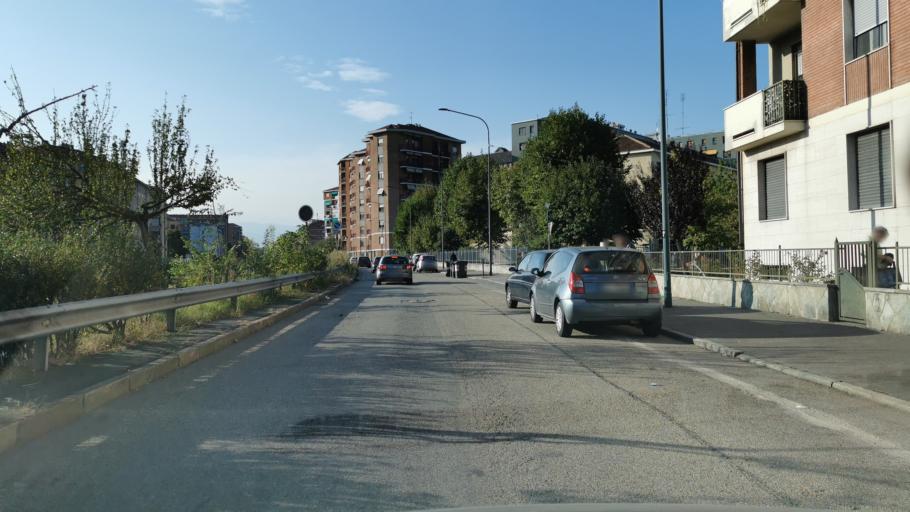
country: IT
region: Piedmont
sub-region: Provincia di Torino
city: Turin
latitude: 45.0919
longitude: 7.7109
